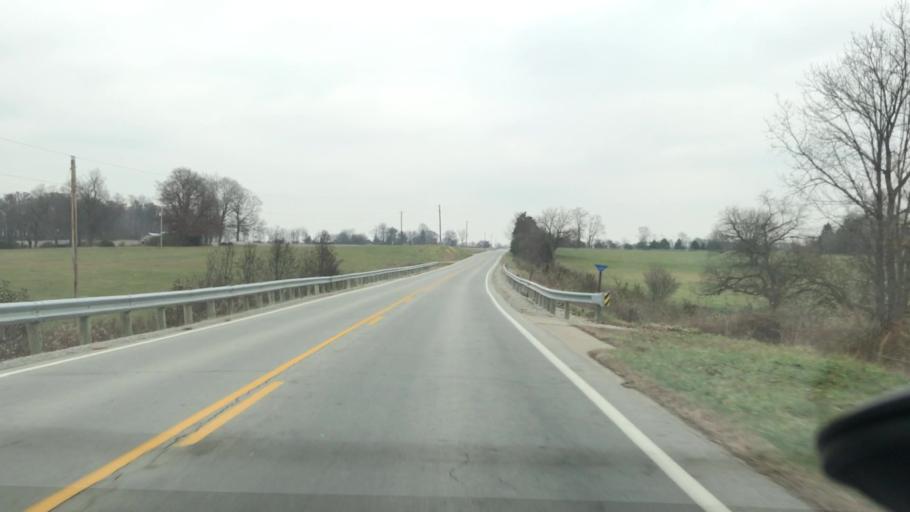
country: US
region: Ohio
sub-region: Greene County
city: Yellow Springs
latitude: 39.7991
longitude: -83.9222
